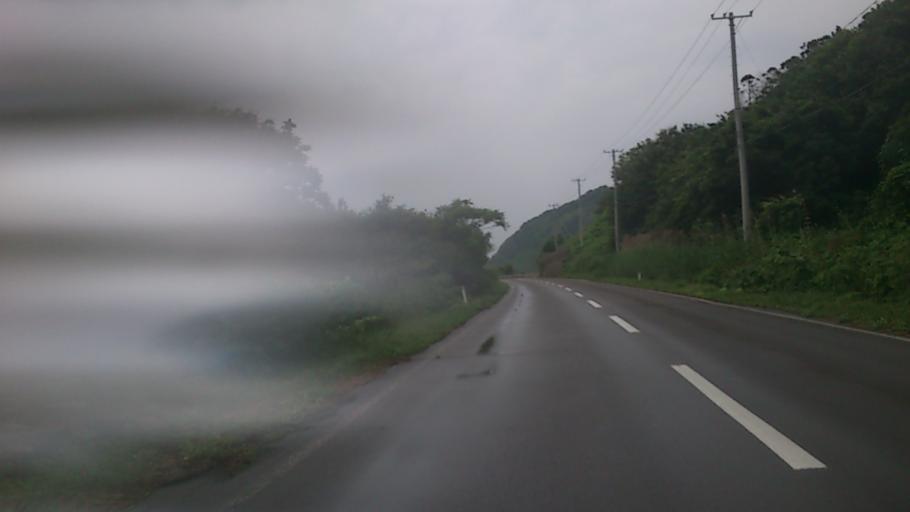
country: JP
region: Akita
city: Noshiromachi
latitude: 40.4721
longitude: 139.9470
